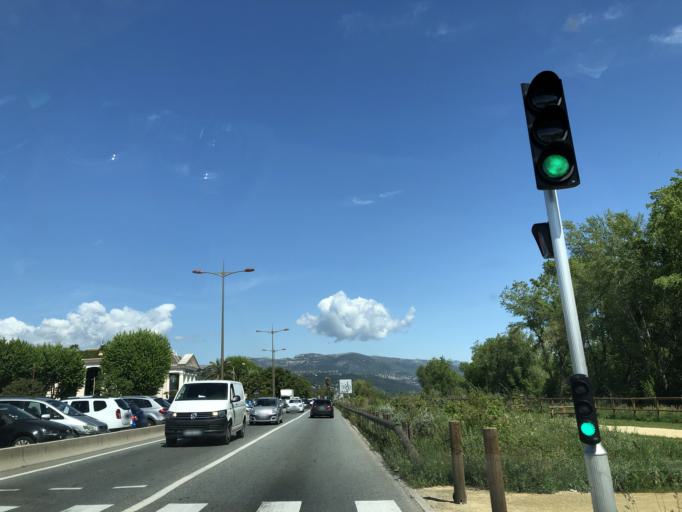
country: FR
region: Provence-Alpes-Cote d'Azur
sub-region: Departement des Alpes-Maritimes
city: Saint-Laurent-du-Var
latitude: 43.6740
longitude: 7.1930
